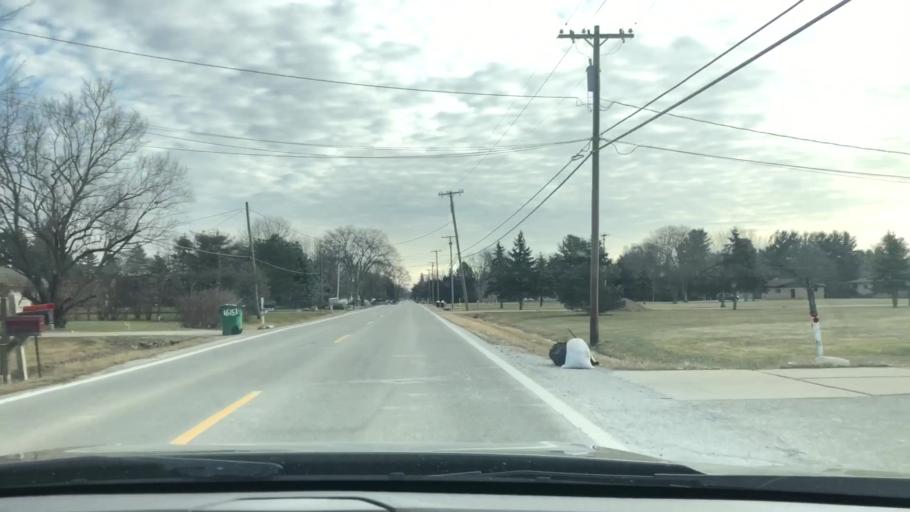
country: US
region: Michigan
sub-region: Macomb County
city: Romeo
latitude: 42.7308
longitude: -82.9660
